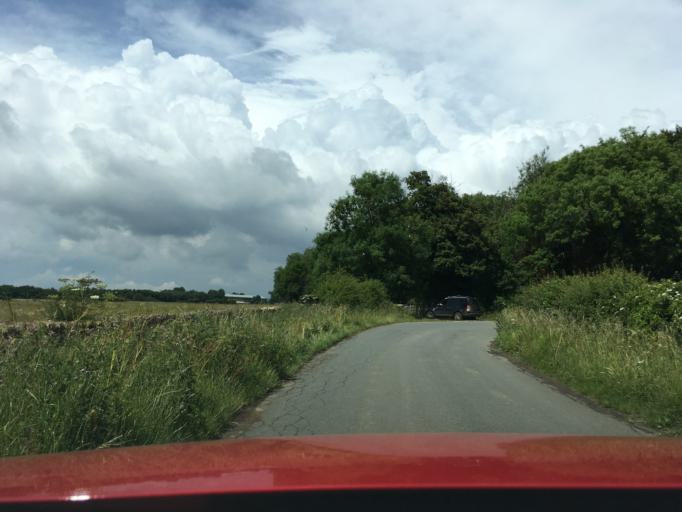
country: GB
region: England
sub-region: Gloucestershire
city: Chalford
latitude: 51.6951
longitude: -2.1256
